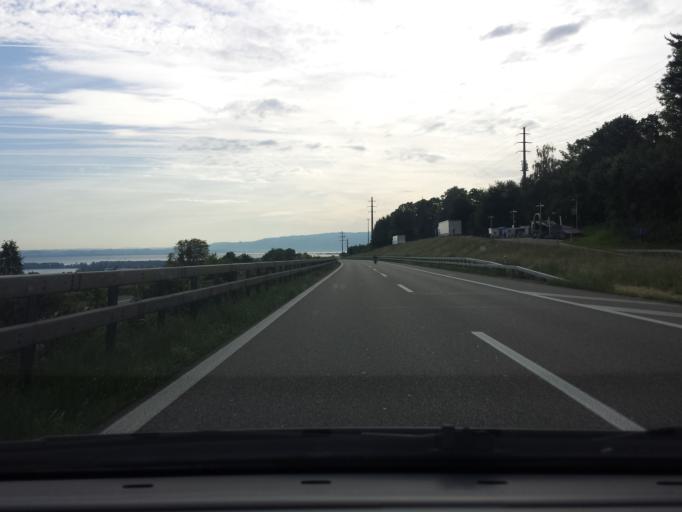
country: CH
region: Saint Gallen
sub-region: Wahlkreis Rorschach
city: Rorschach
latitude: 47.4724
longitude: 9.5160
